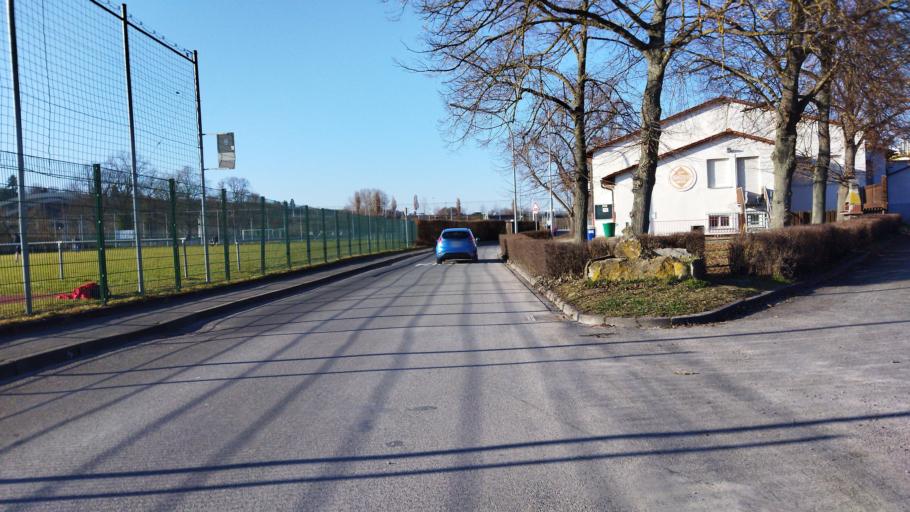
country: DE
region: Bavaria
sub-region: Regierungsbezirk Unterfranken
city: Kitzingen
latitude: 49.7430
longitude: 10.1648
